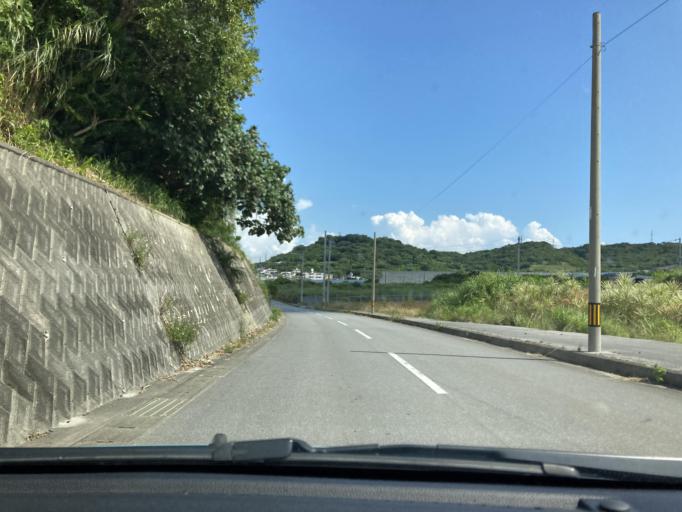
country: JP
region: Okinawa
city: Tomigusuku
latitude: 26.1575
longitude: 127.7549
